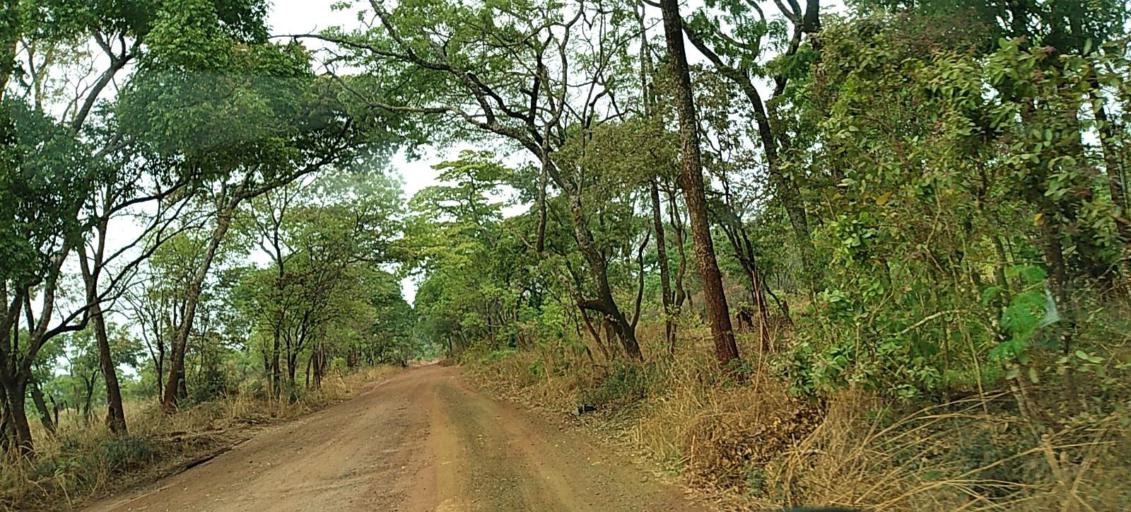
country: ZM
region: North-Western
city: Solwezi
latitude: -12.3196
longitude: 26.5219
